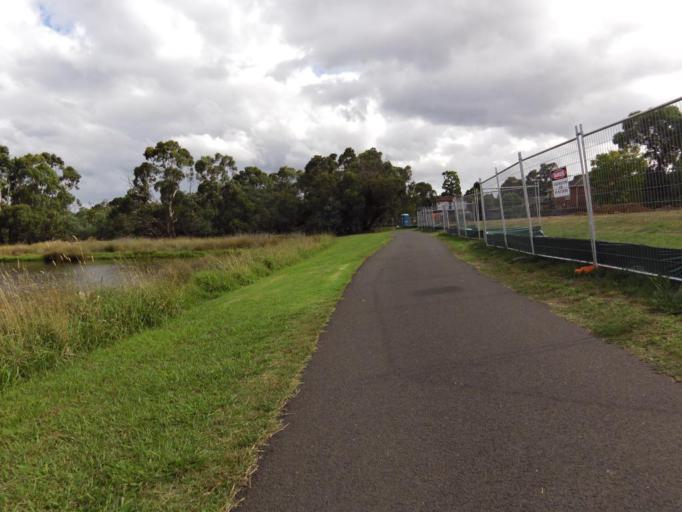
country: AU
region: Victoria
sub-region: Knox
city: Knoxfield
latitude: -37.8788
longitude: 145.2472
